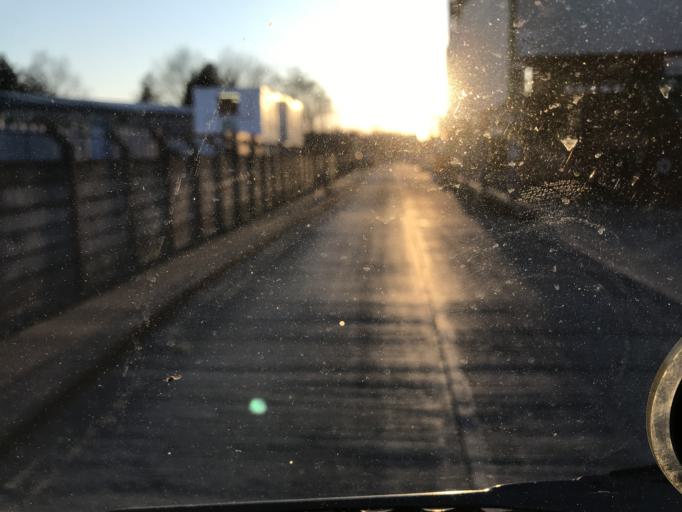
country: GB
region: England
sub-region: City and Borough of Salford
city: Eccles
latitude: 53.4775
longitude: -2.3274
